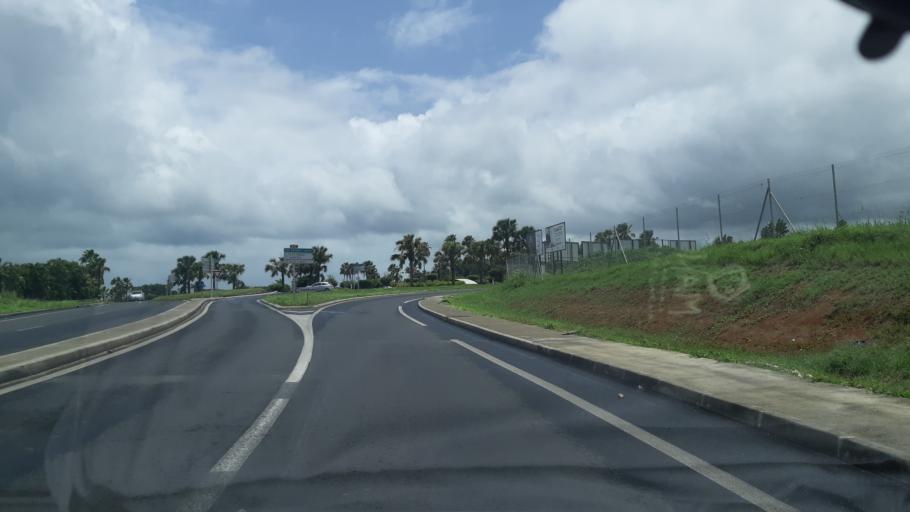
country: GP
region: Guadeloupe
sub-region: Guadeloupe
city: Les Abymes
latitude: 16.2623
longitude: -61.5137
